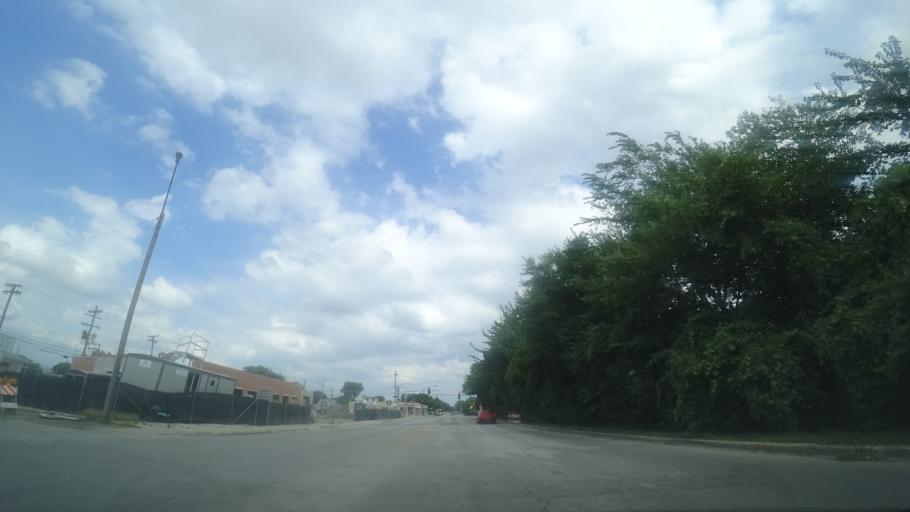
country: US
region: Illinois
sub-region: Cook County
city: Harwood Heights
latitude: 41.9684
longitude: -87.7893
